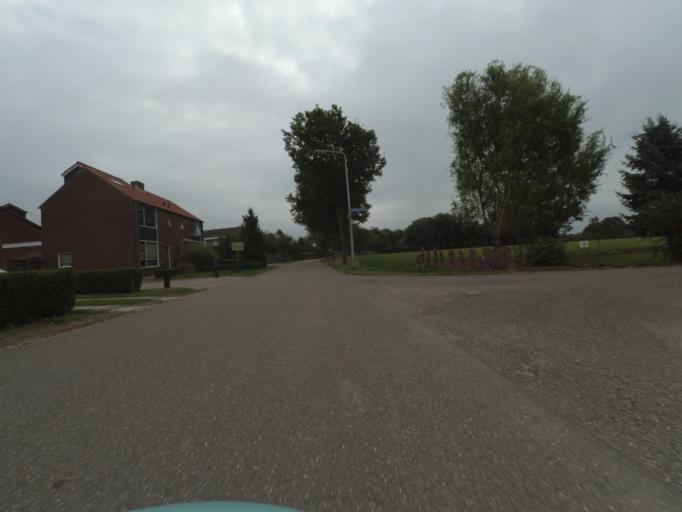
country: NL
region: Gelderland
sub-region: Gemeente Geldermalsen
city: Geldermalsen
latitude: 51.9301
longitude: 5.3095
